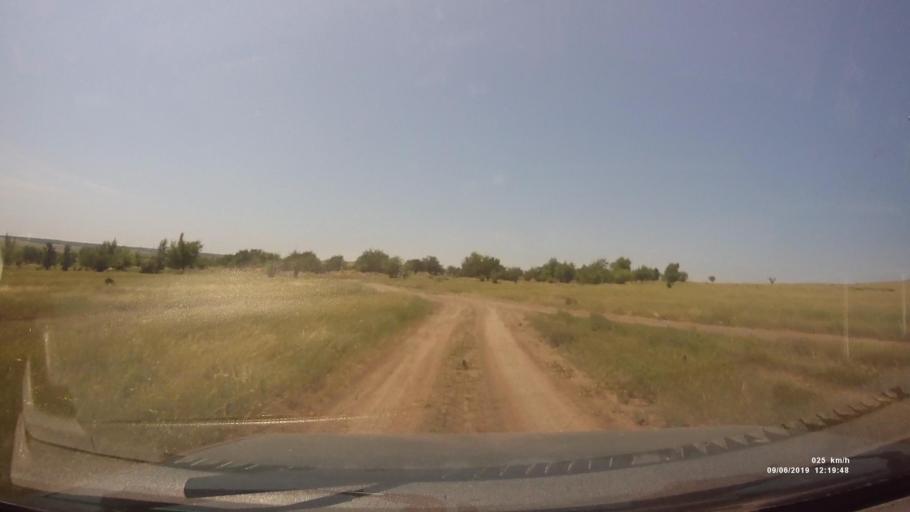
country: RU
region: Rostov
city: Kamensk-Shakhtinskiy
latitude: 48.2523
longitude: 40.3042
